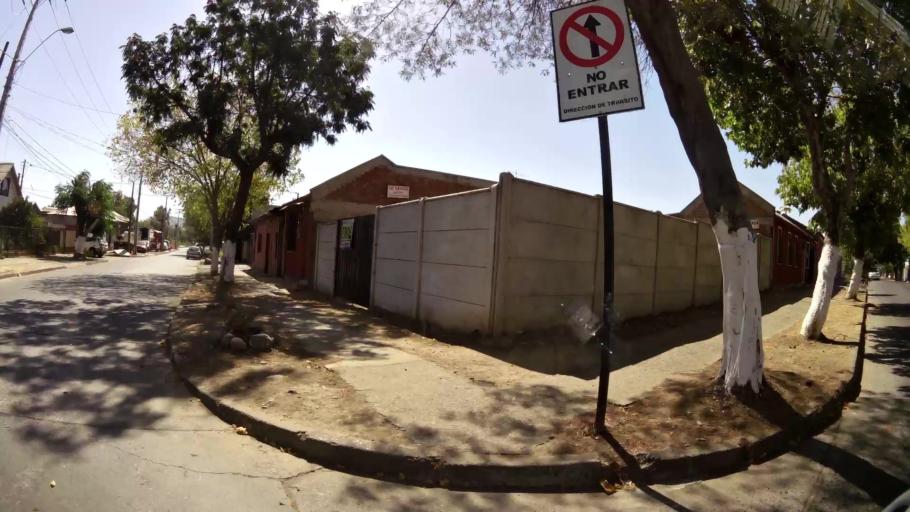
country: CL
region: Maule
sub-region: Provincia de Talca
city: Talca
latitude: -35.4342
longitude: -71.6634
